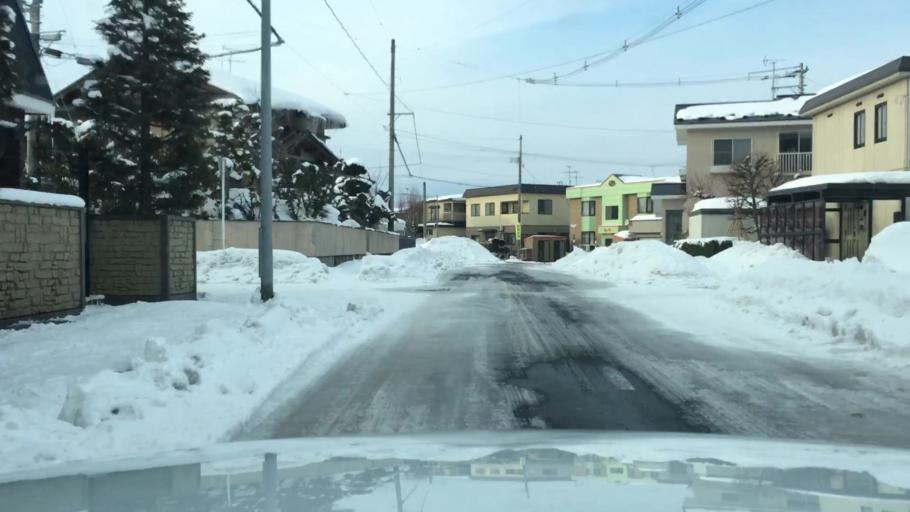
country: JP
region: Aomori
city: Hirosaki
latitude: 40.5782
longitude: 140.4885
